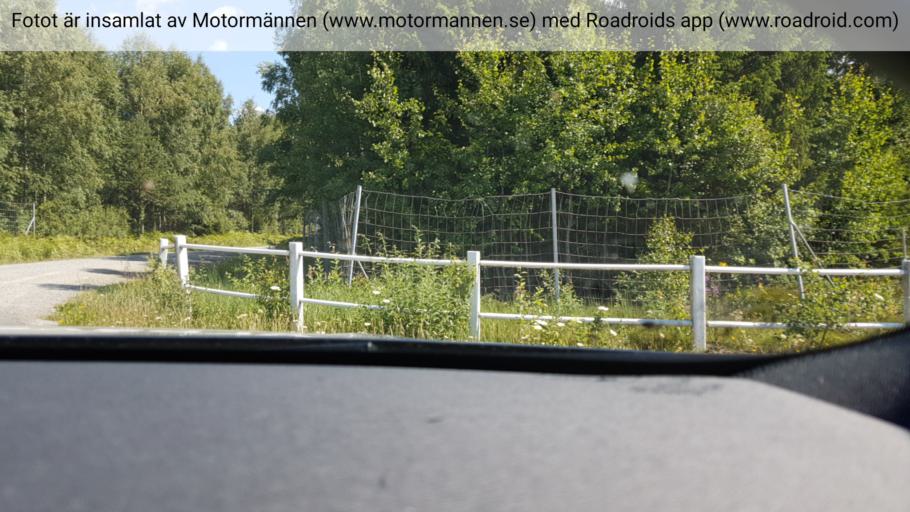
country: SE
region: Vaestra Goetaland
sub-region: Lidkopings Kommun
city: Lidkoping
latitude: 58.4750
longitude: 13.2069
